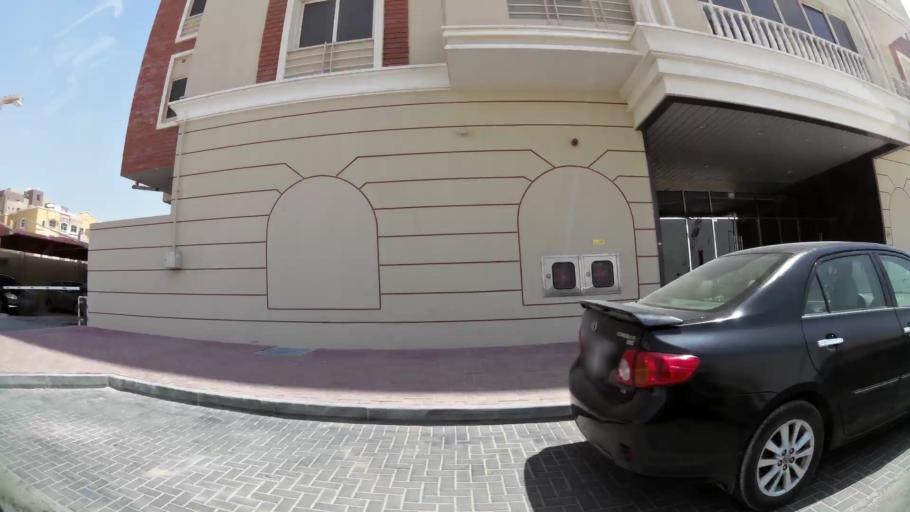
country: AE
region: Ash Shariqah
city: Sharjah
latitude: 25.1815
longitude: 55.4079
